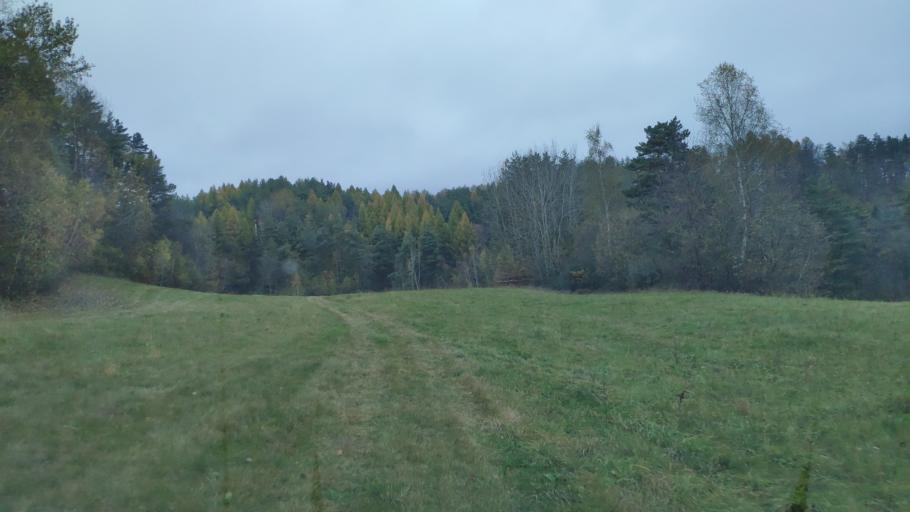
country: SK
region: Presovsky
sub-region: Okres Presov
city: Presov
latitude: 48.9328
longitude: 21.0975
